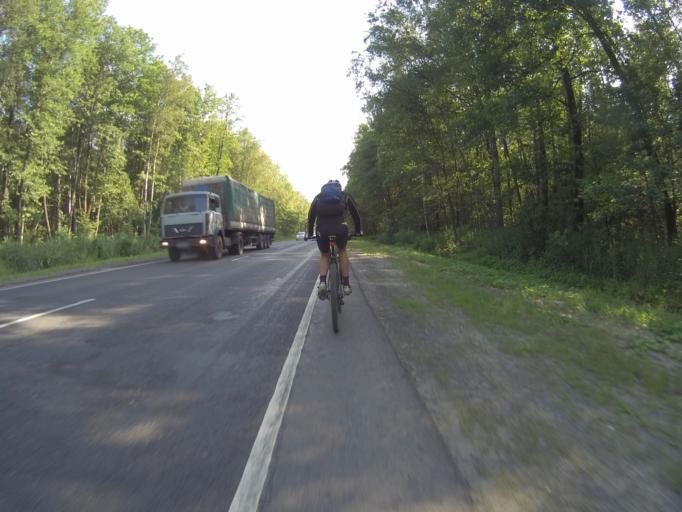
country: RU
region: Ivanovo
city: Nerl'
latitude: 56.6203
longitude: 40.5637
